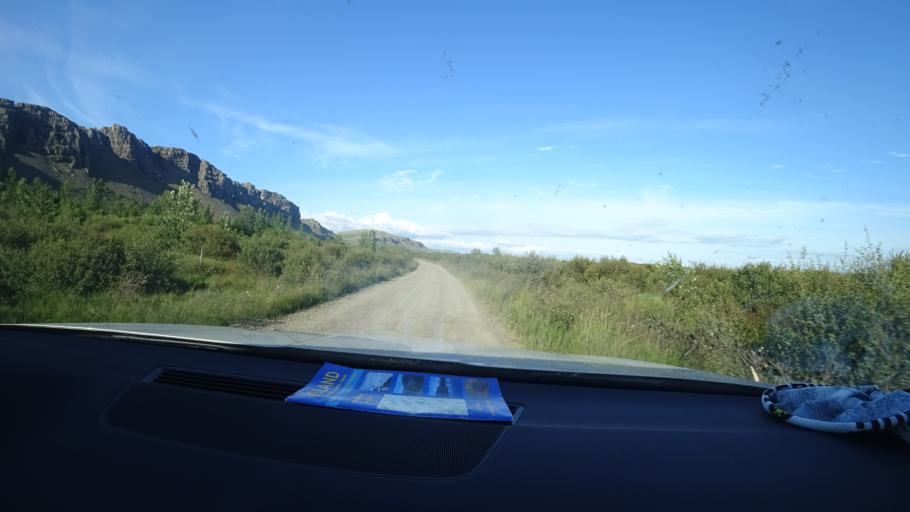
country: IS
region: West
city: Borgarnes
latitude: 64.6927
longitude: -21.9281
